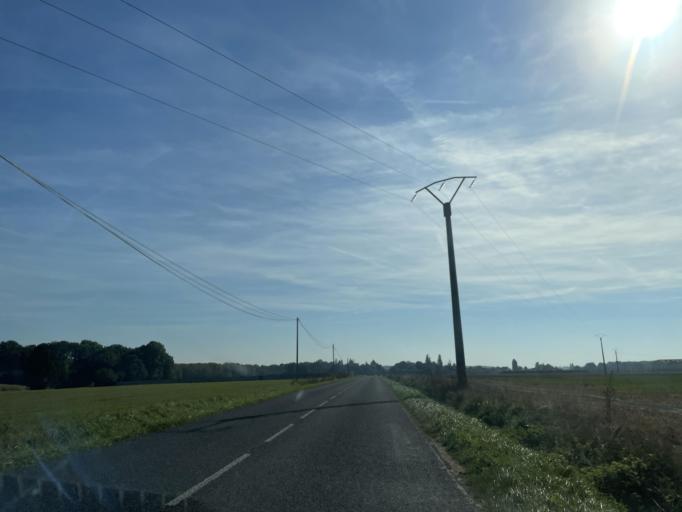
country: FR
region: Ile-de-France
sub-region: Departement de Seine-et-Marne
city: Saint-Jean-les-Deux-Jumeaux
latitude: 48.9053
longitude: 3.0282
